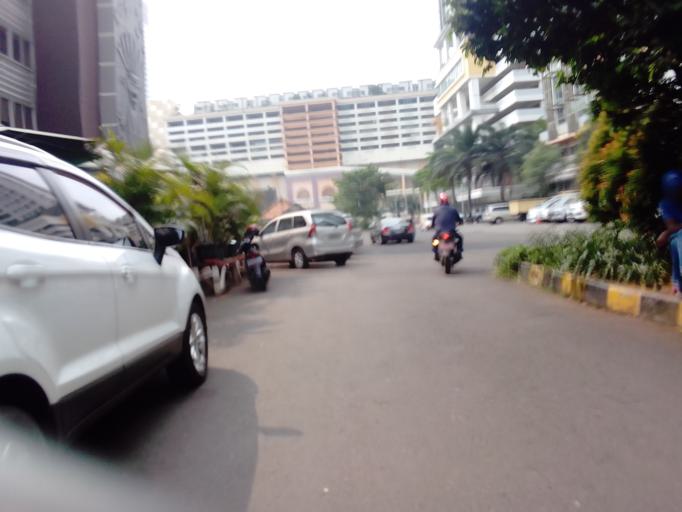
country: ID
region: Jakarta Raya
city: Jakarta
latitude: -6.1972
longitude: 106.8161
